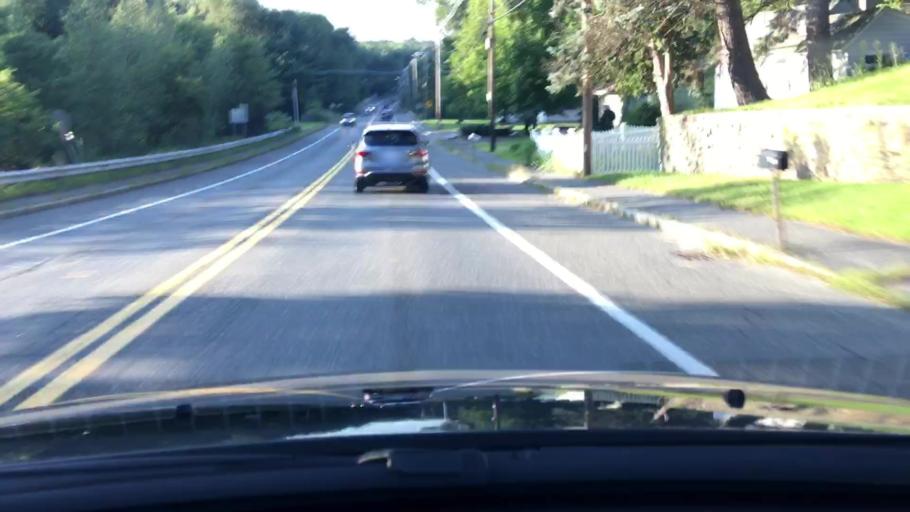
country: US
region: Massachusetts
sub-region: Worcester County
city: Shrewsbury
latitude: 42.3081
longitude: -71.7171
